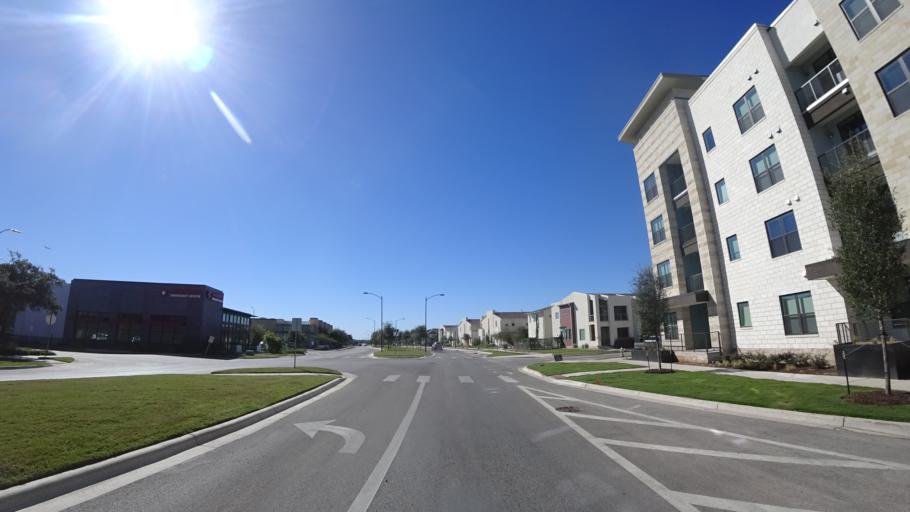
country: US
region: Texas
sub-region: Travis County
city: Austin
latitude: 30.3015
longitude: -97.7003
